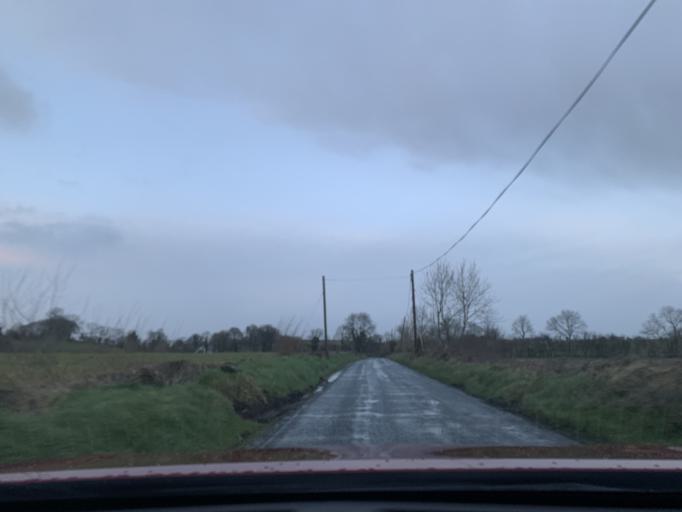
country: IE
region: Connaught
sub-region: Sligo
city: Ballymote
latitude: 54.0408
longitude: -8.6096
